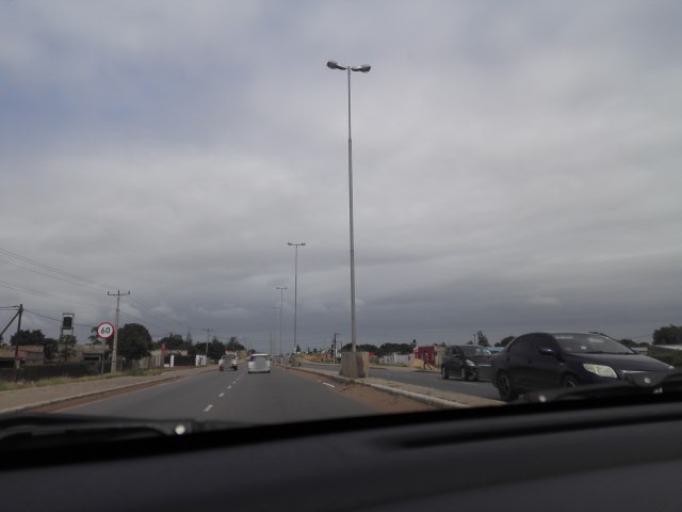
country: MZ
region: Maputo City
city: Maputo
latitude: -25.8259
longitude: 32.6000
